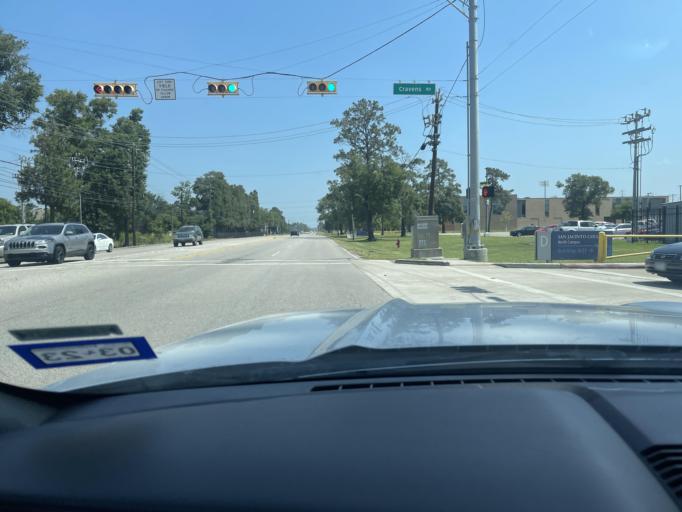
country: US
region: Texas
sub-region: Harris County
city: Cloverleaf
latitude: 29.8110
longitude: -95.1824
